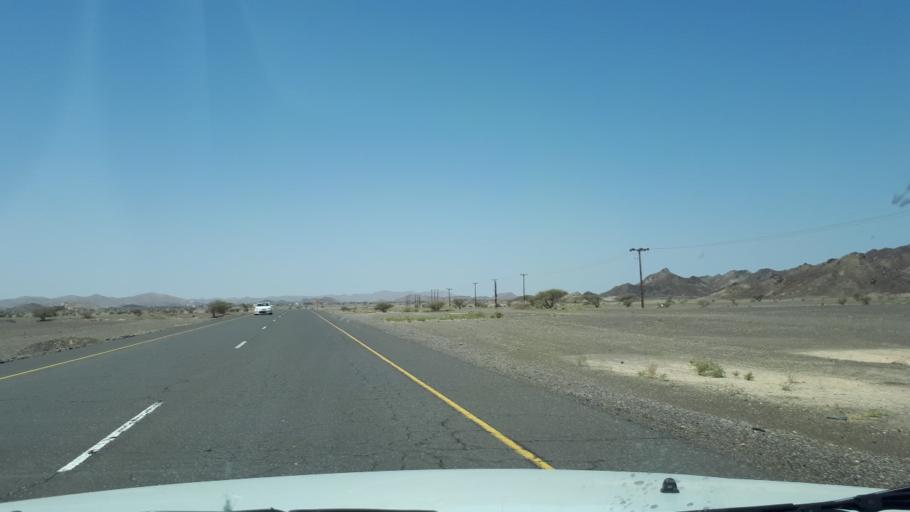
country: OM
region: Ash Sharqiyah
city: Ibra'
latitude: 22.6217
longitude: 58.4469
